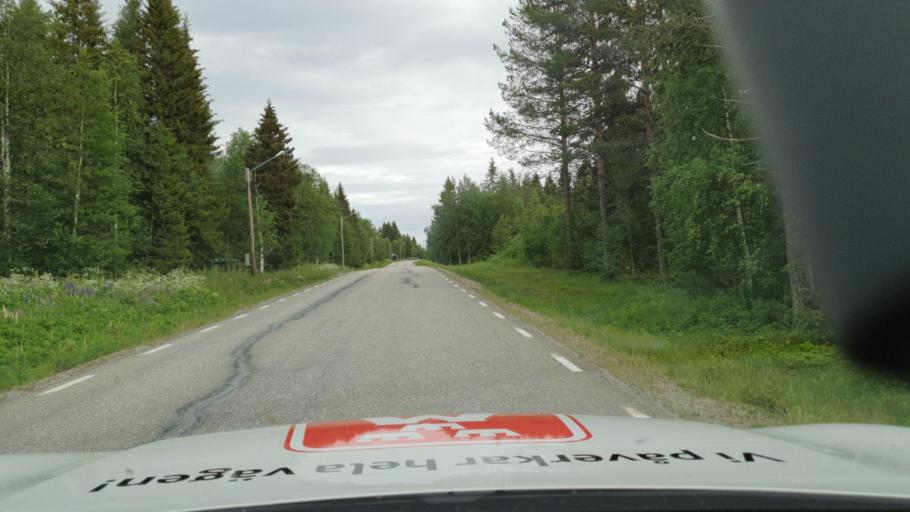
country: SE
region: Vaesterbotten
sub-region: Lycksele Kommun
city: Soderfors
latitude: 64.3631
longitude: 18.0969
